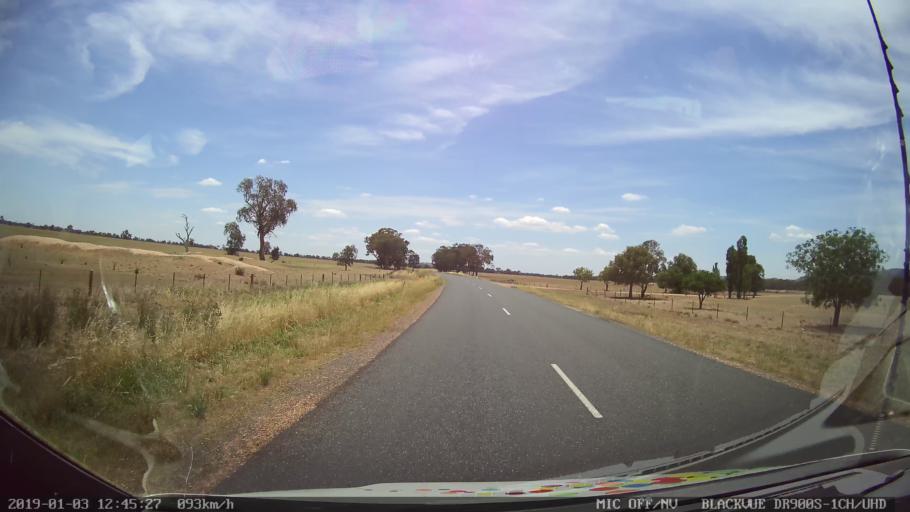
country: AU
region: New South Wales
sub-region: Weddin
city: Grenfell
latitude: -33.7494
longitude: 148.2235
